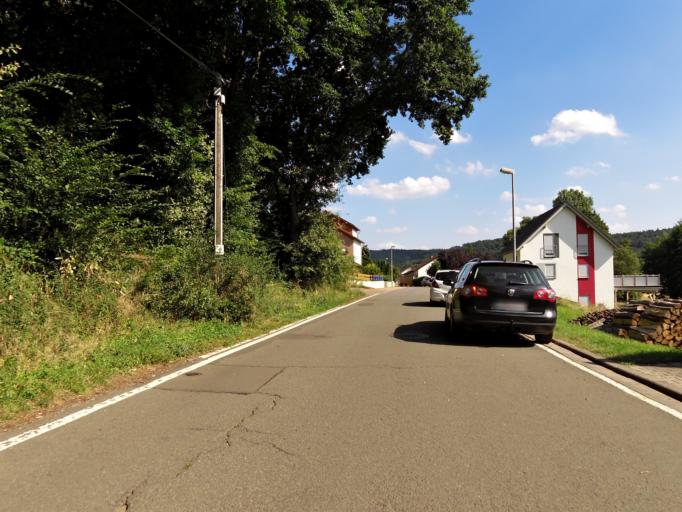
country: DE
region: Rheinland-Pfalz
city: Ramsen
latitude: 49.5406
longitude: 7.9992
